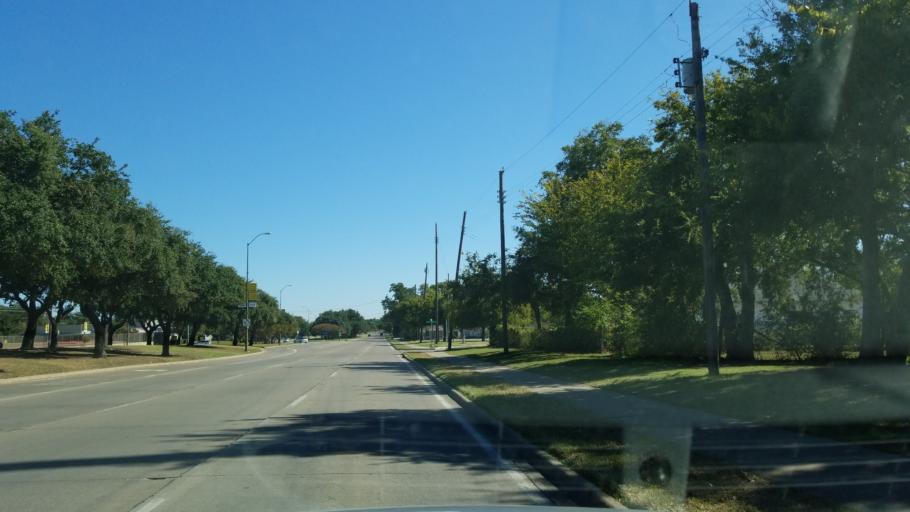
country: US
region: Texas
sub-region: Dallas County
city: Dallas
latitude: 32.7725
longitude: -96.7600
